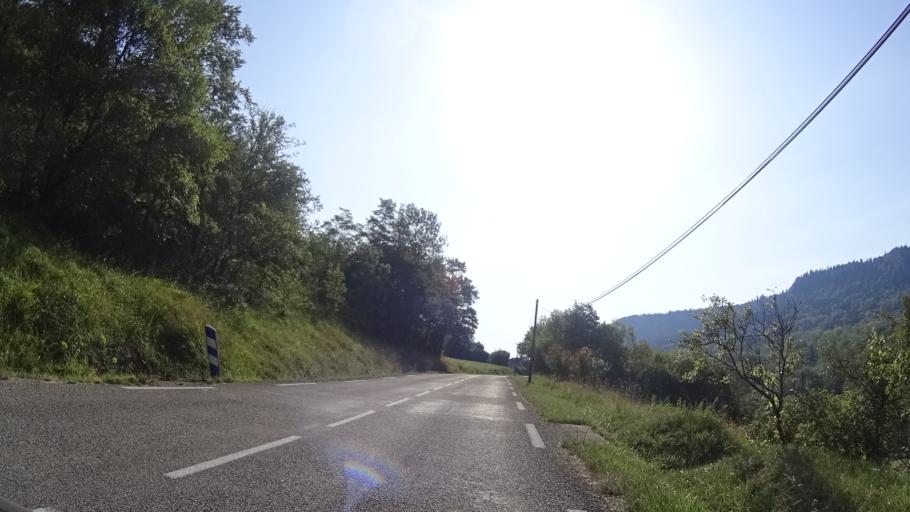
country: FR
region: Midi-Pyrenees
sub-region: Departement de l'Ariege
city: Belesta
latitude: 42.9111
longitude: 1.9598
